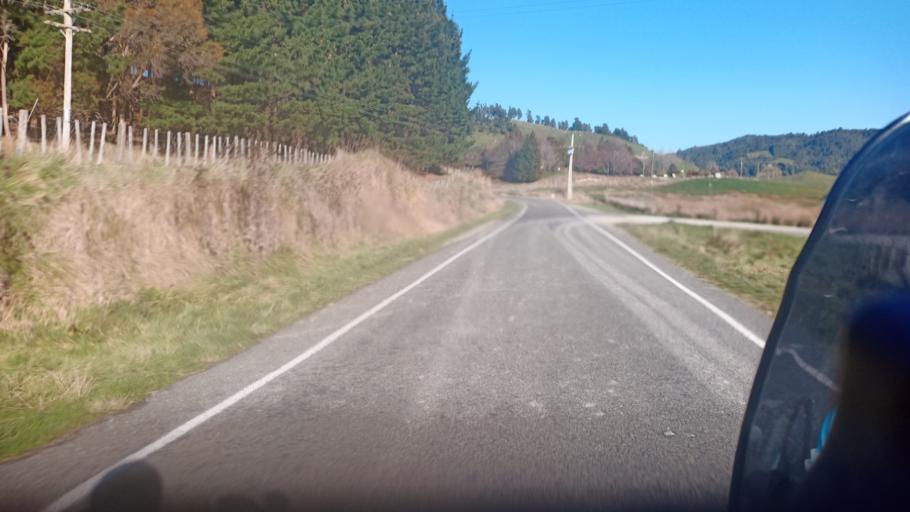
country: NZ
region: Gisborne
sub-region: Gisborne District
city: Gisborne
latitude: -38.5796
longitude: 177.5542
